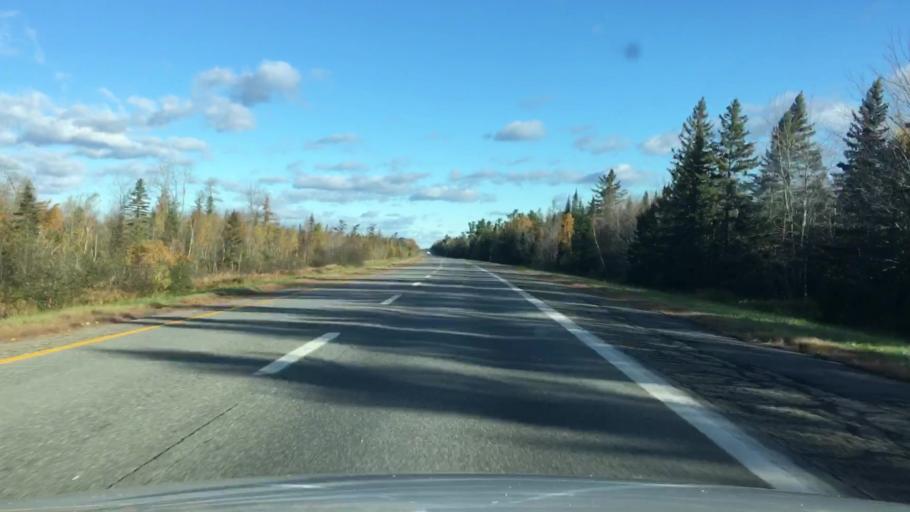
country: US
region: Maine
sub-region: Penobscot County
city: Greenbush
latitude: 45.0548
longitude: -68.6874
